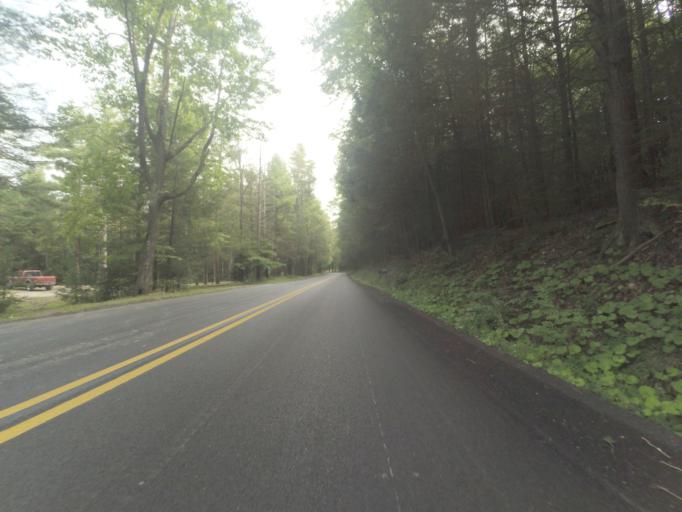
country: US
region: Pennsylvania
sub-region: Centre County
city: Milesburg
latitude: 41.0366
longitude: -77.7238
